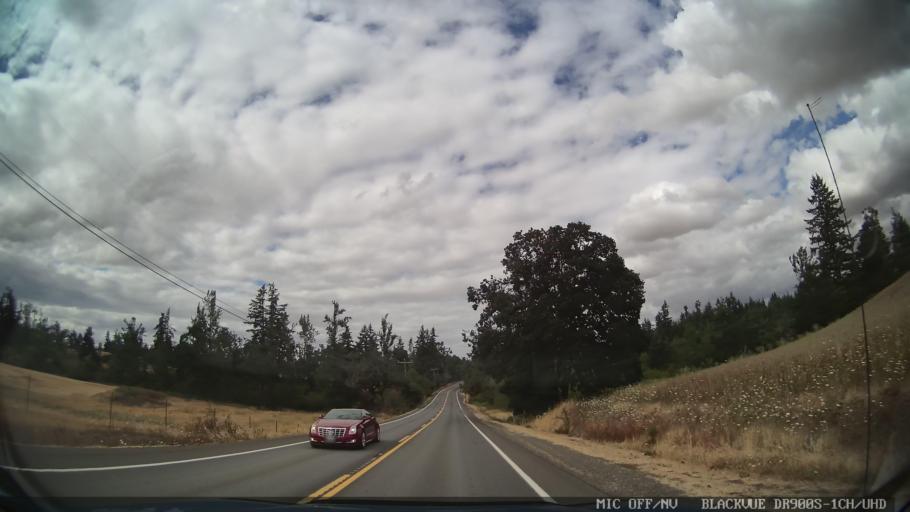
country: US
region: Oregon
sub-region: Marion County
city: Sublimity
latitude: 44.8467
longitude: -122.7945
